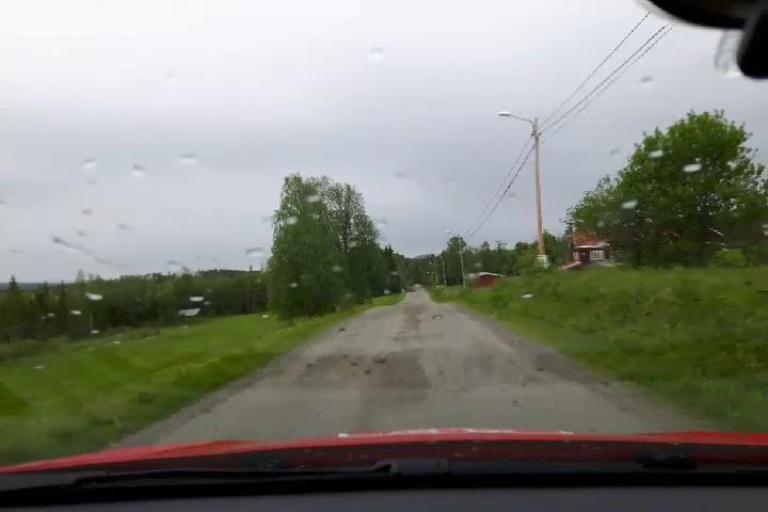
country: SE
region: Jaemtland
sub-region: Bergs Kommun
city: Hoverberg
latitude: 62.7413
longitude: 14.4569
